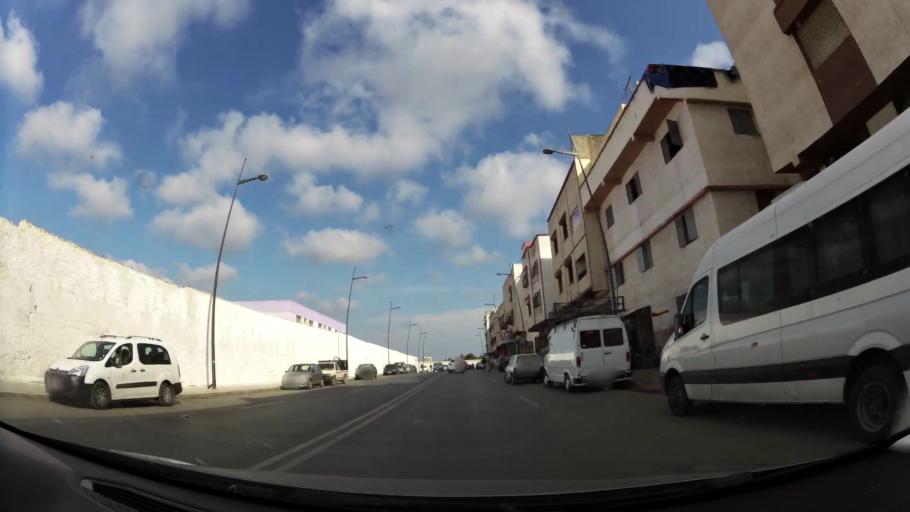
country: MA
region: Rabat-Sale-Zemmour-Zaer
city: Sale
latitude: 34.0552
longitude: -6.7741
